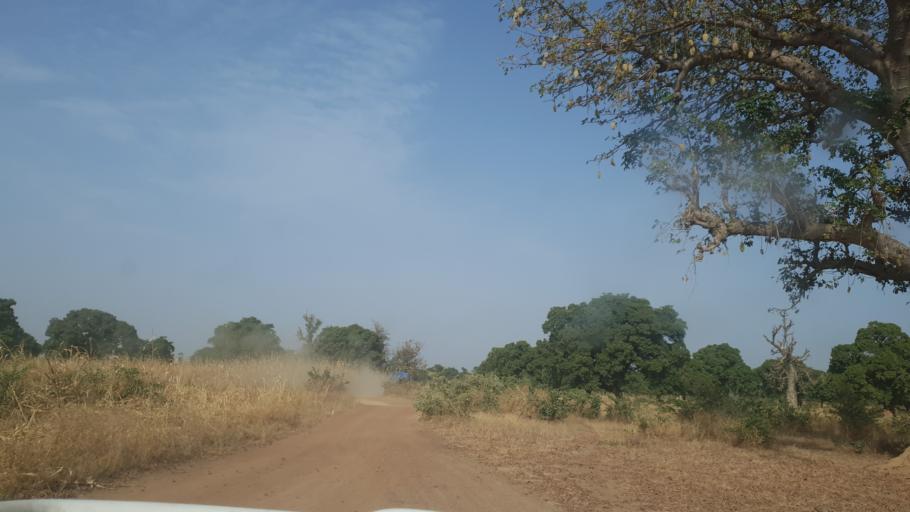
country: ML
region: Segou
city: Baroueli
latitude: 13.3478
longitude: -6.9441
